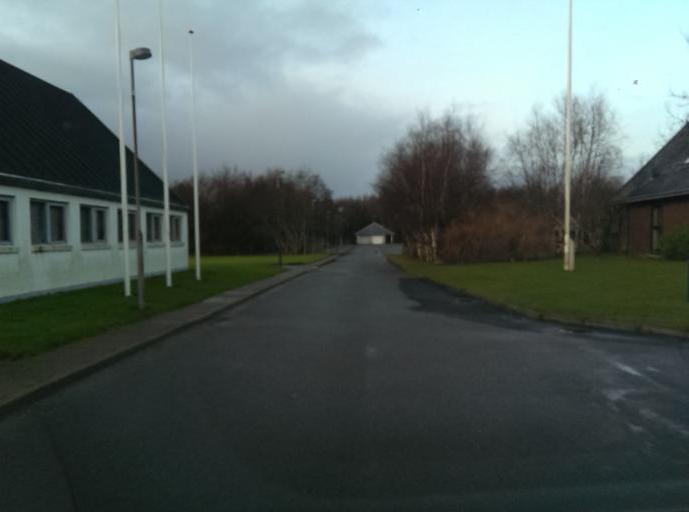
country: DK
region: South Denmark
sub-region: Varde Kommune
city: Varde
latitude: 55.6324
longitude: 8.4784
